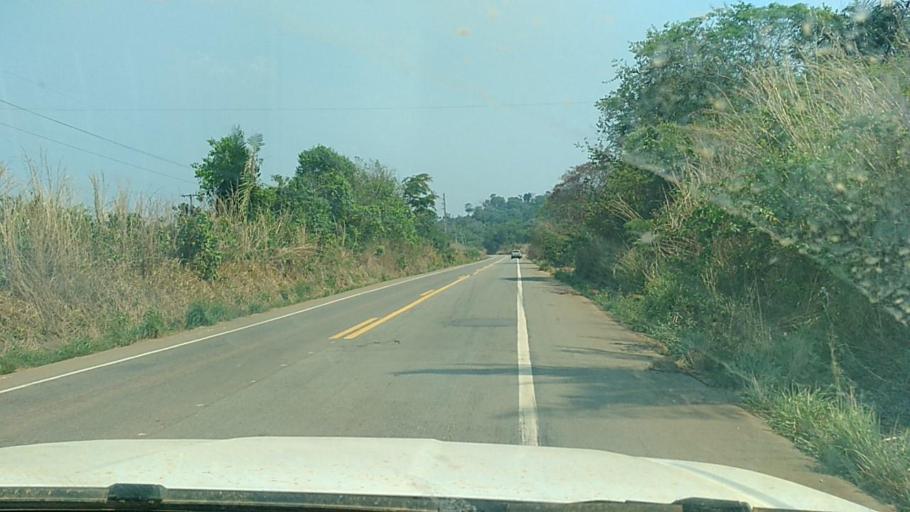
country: BR
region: Rondonia
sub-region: Porto Velho
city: Porto Velho
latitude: -8.7862
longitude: -63.4718
